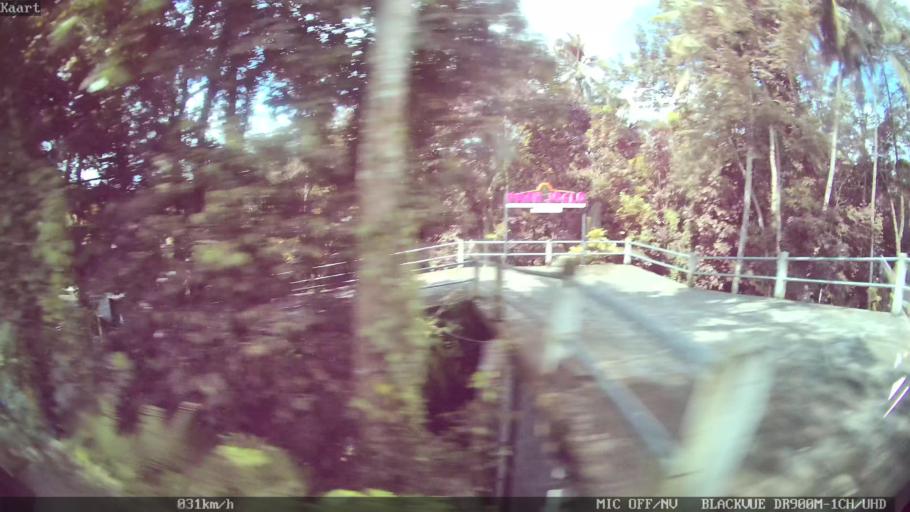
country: ID
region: Bali
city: Banjar Abuan
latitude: -8.4633
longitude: 115.3251
